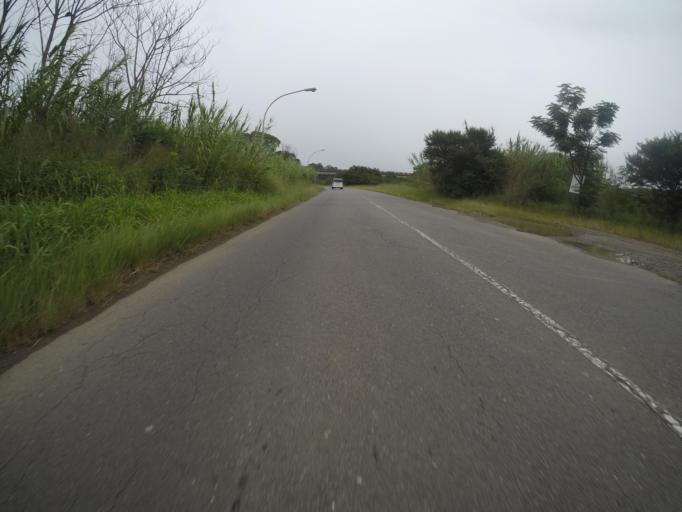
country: ZA
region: Eastern Cape
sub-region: Buffalo City Metropolitan Municipality
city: East London
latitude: -32.9671
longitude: 27.9193
